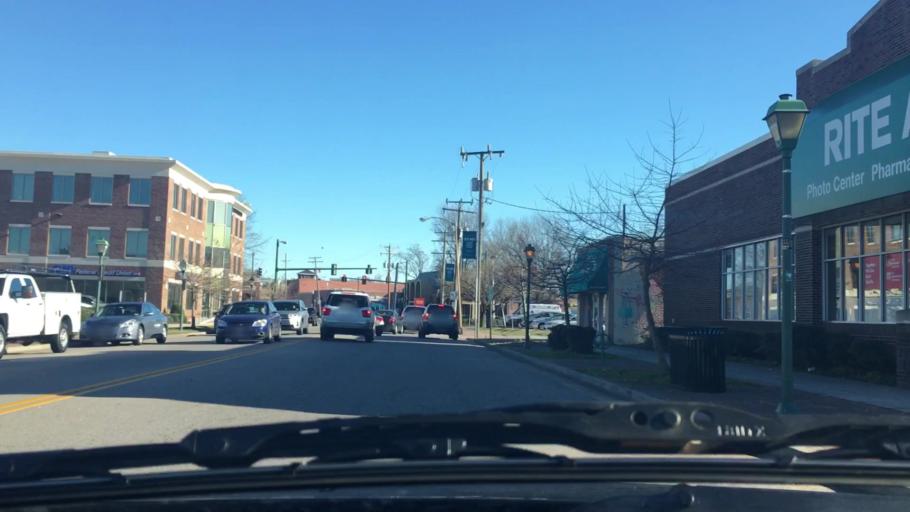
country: US
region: Virginia
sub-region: City of Norfolk
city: Norfolk
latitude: 36.8695
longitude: -76.2930
